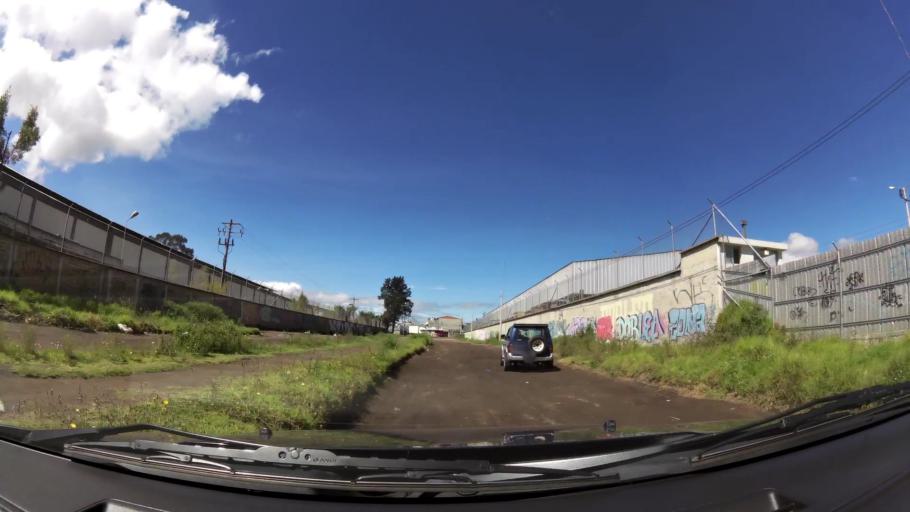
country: EC
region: Pichincha
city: Quito
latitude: -0.3020
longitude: -78.5477
